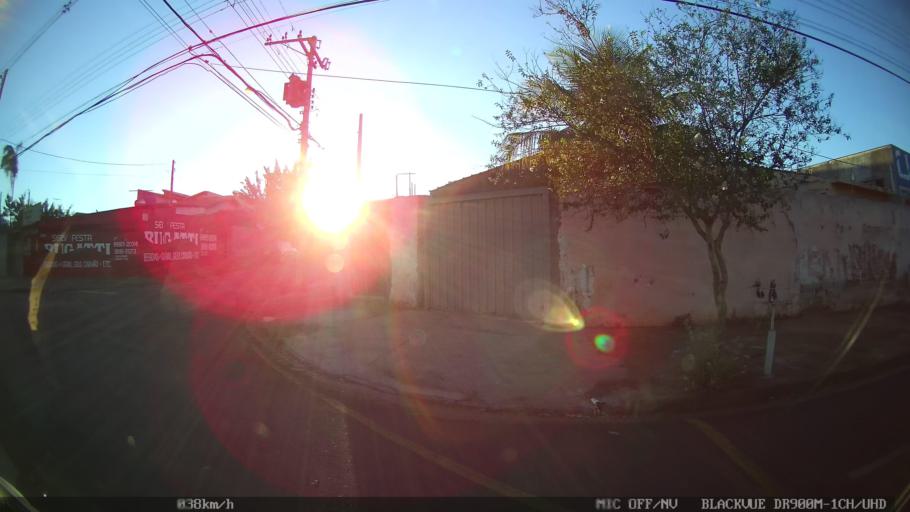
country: BR
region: Sao Paulo
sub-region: Sao Jose Do Rio Preto
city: Sao Jose do Rio Preto
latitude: -20.7789
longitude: -49.3577
